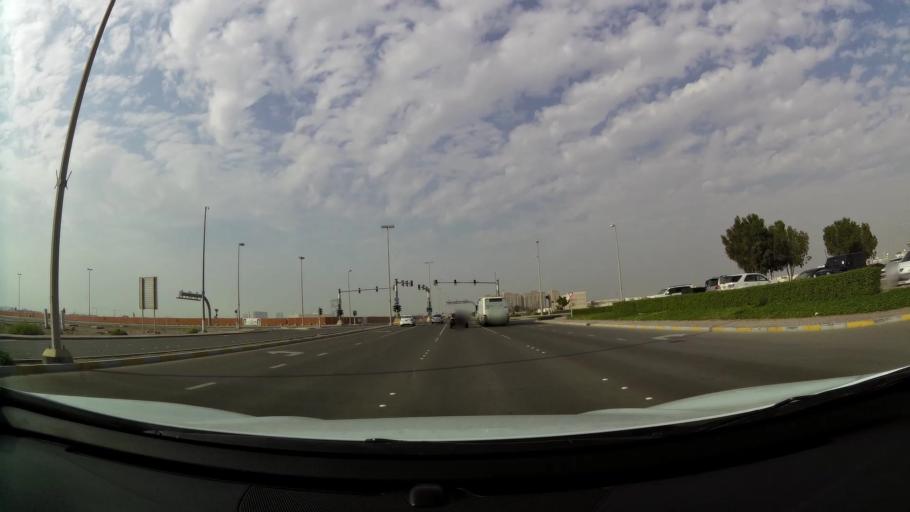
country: AE
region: Abu Dhabi
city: Abu Dhabi
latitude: 24.3602
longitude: 54.5371
